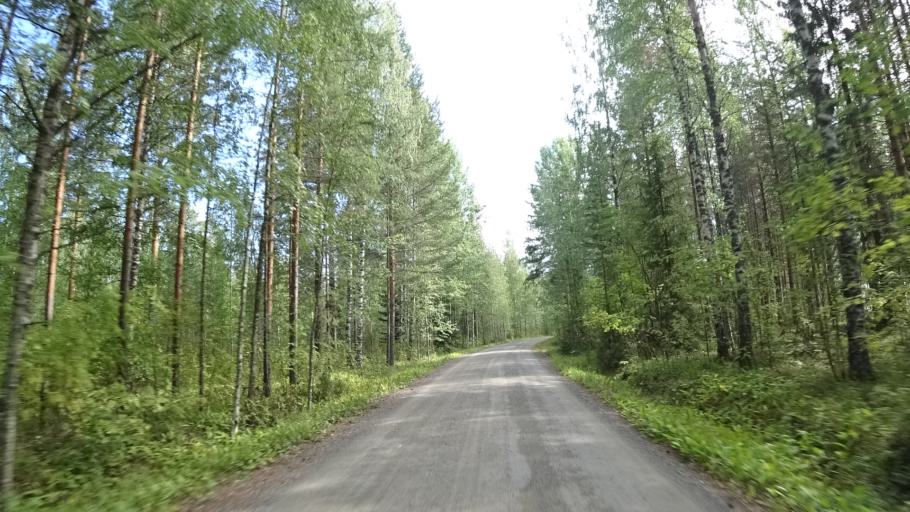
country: FI
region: North Karelia
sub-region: Joensuu
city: Pyhaeselkae
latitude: 62.3859
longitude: 29.7976
